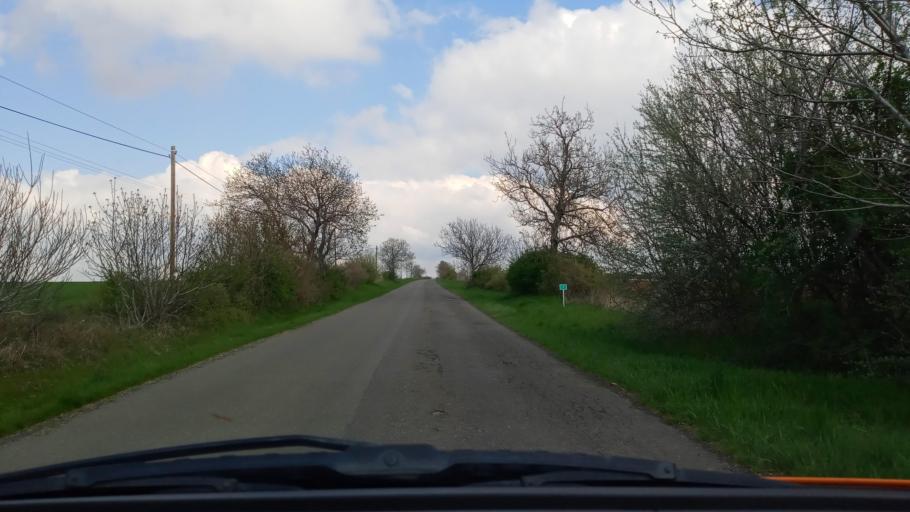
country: HU
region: Baranya
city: Pecsvarad
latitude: 46.0987
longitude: 18.4985
